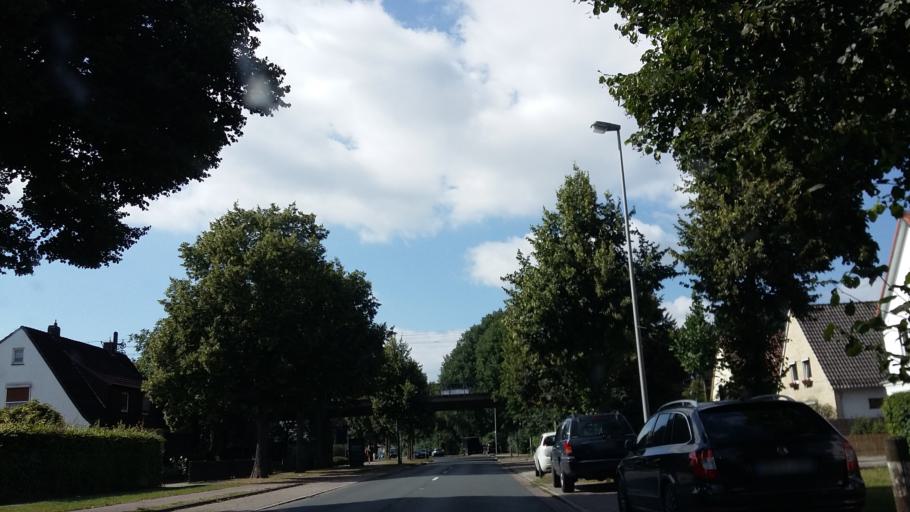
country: DE
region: Bremen
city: Bremen
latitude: 53.0431
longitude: 8.8266
